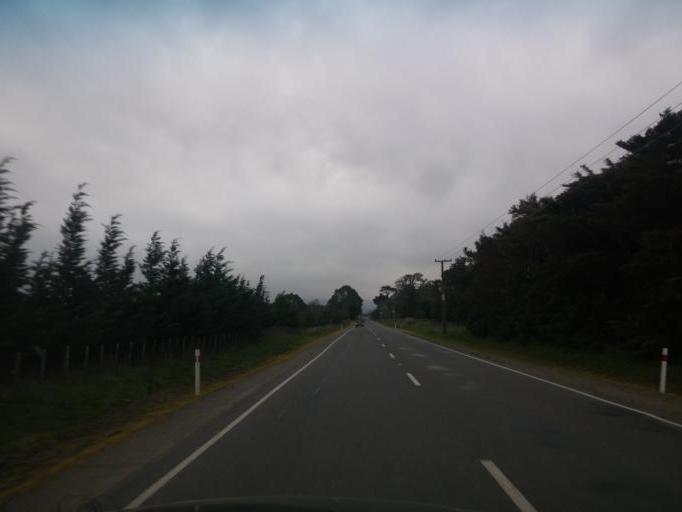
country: NZ
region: Wellington
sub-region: South Wairarapa District
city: Waipawa
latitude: -41.1481
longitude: 175.3658
